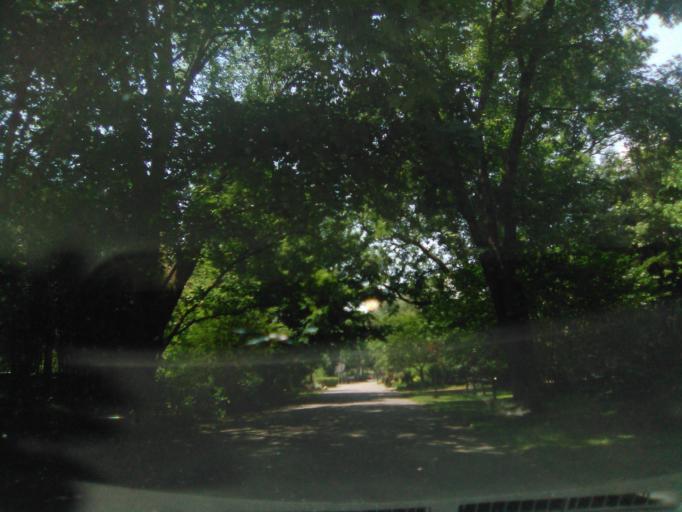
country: US
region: Tennessee
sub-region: Davidson County
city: Belle Meade
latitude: 36.1332
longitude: -86.8369
